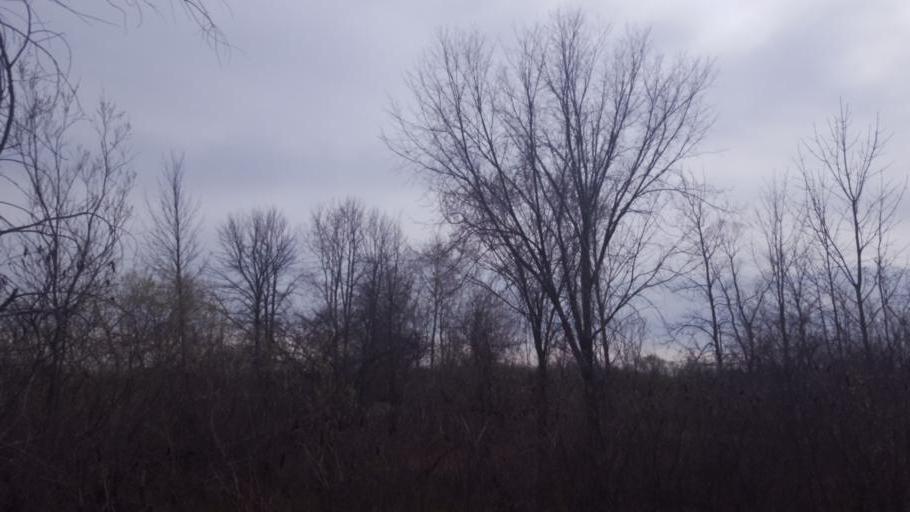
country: US
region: Michigan
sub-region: Clare County
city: Clare
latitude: 43.8727
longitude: -84.7600
